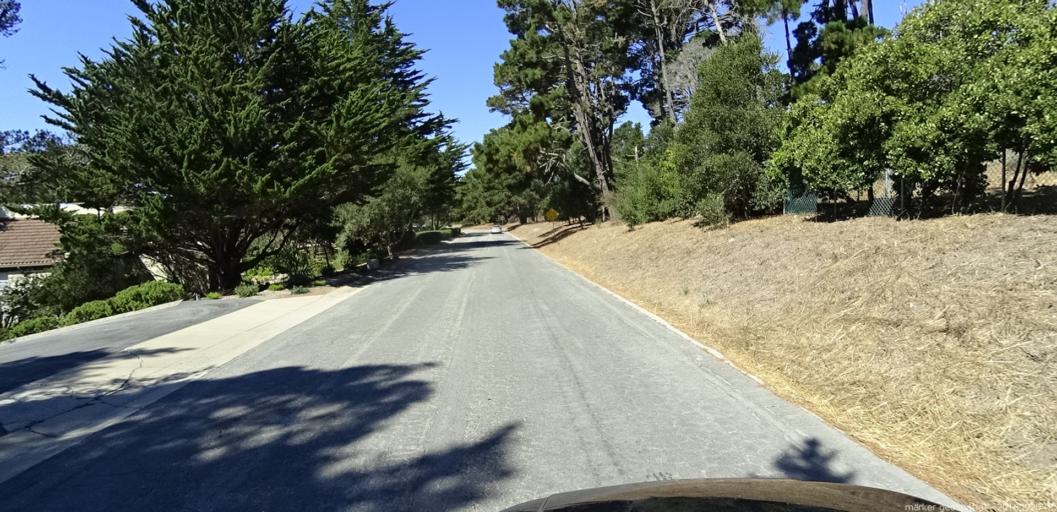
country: US
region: California
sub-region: Monterey County
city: Carmel-by-the-Sea
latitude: 36.5677
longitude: -121.9096
